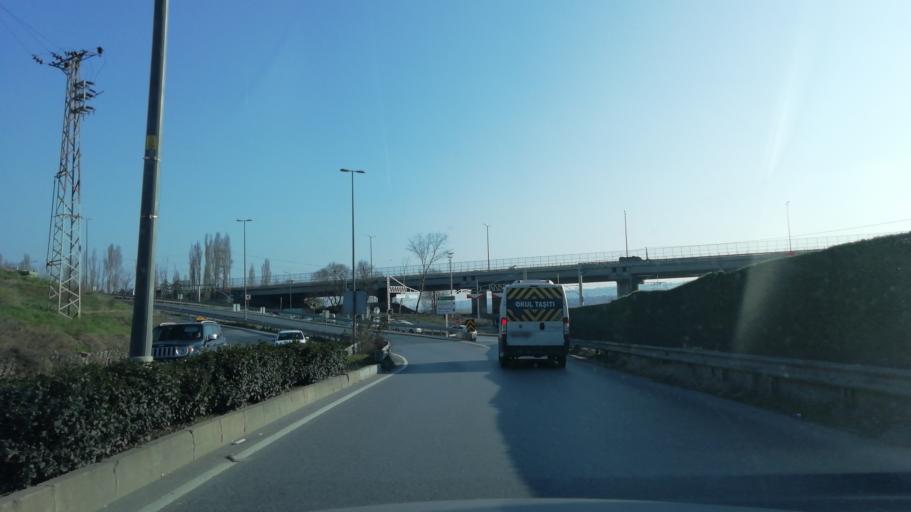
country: TR
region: Istanbul
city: Esenyurt
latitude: 41.0608
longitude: 28.7008
